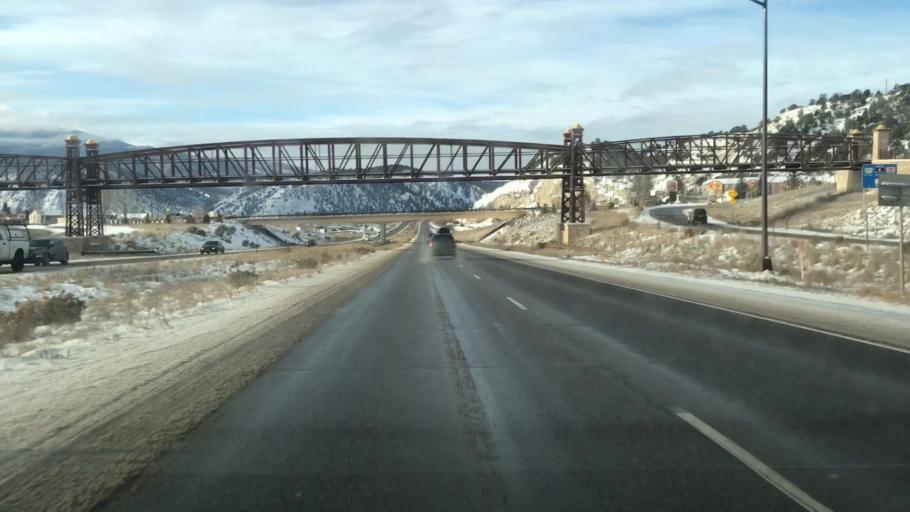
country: US
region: Colorado
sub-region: Eagle County
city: Eagle
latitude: 39.6613
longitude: -106.8260
